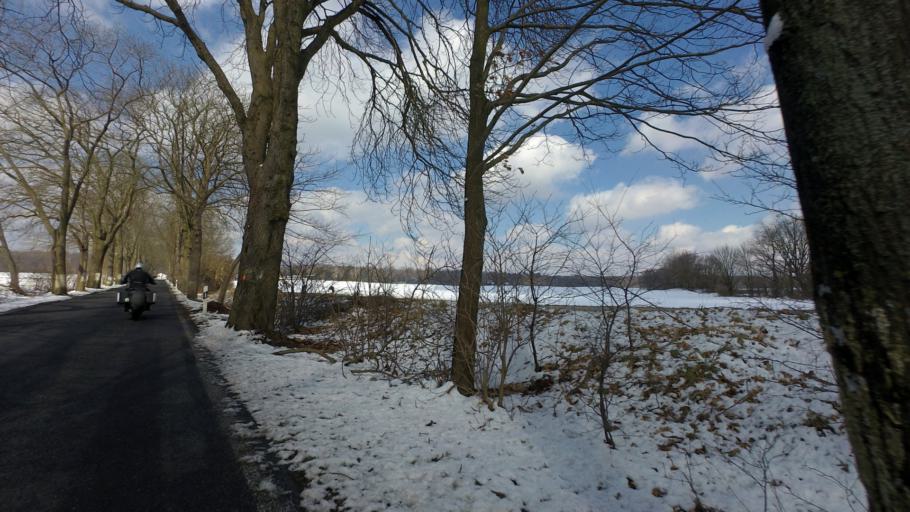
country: DE
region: Brandenburg
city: Joachimsthal
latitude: 52.9036
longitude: 13.7106
